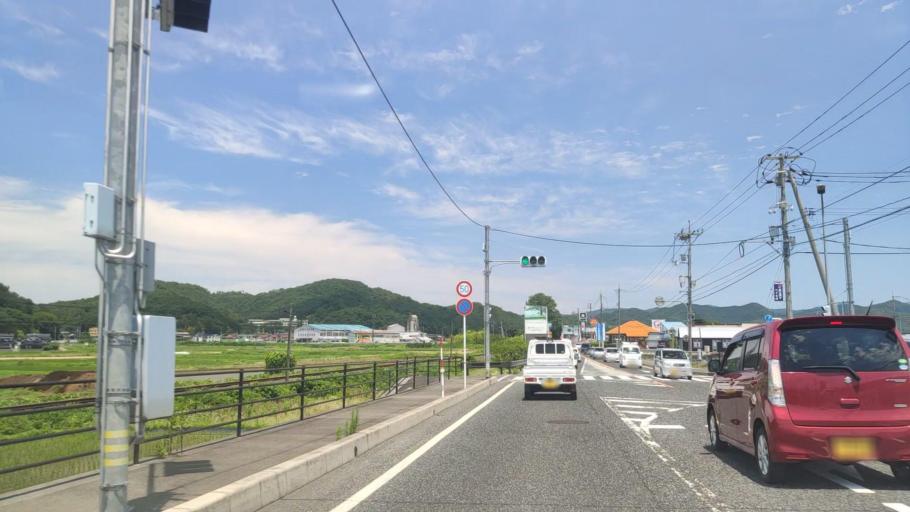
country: JP
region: Tottori
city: Tottori
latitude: 35.4201
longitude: 134.2597
